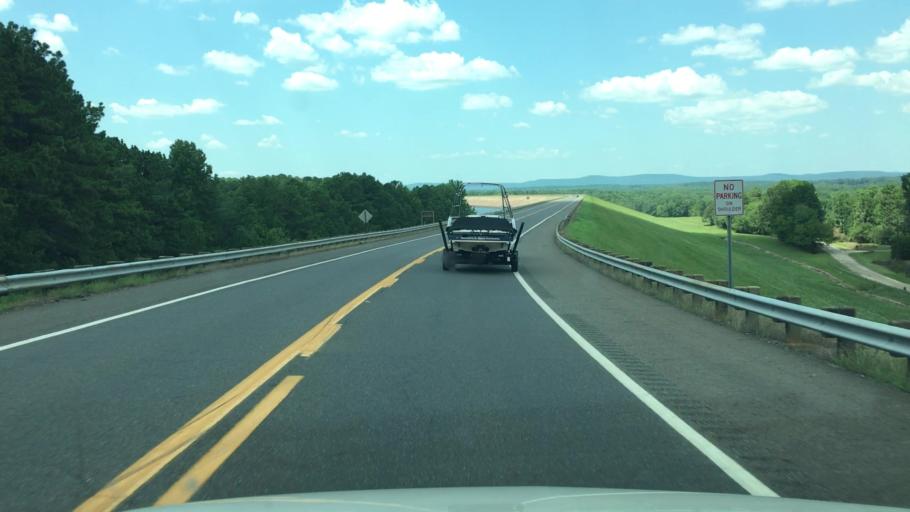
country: US
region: Arkansas
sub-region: Clark County
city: Arkadelphia
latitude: 34.2329
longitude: -93.1001
